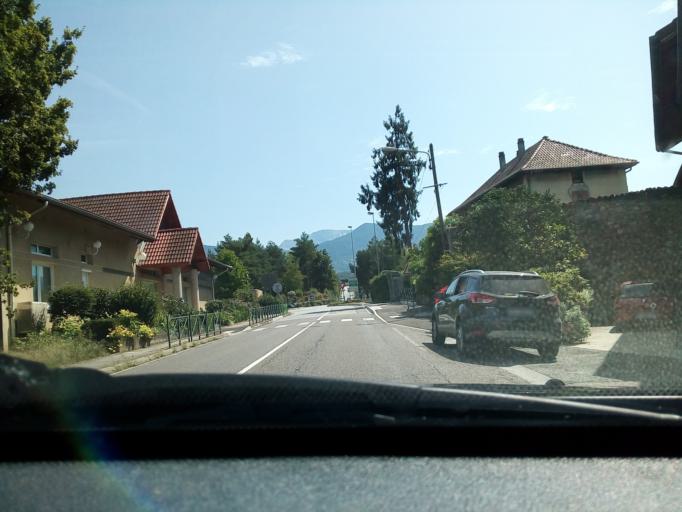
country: FR
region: Rhone-Alpes
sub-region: Departement de l'Isere
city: Brie-et-Angonnes
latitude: 45.1360
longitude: 5.7706
